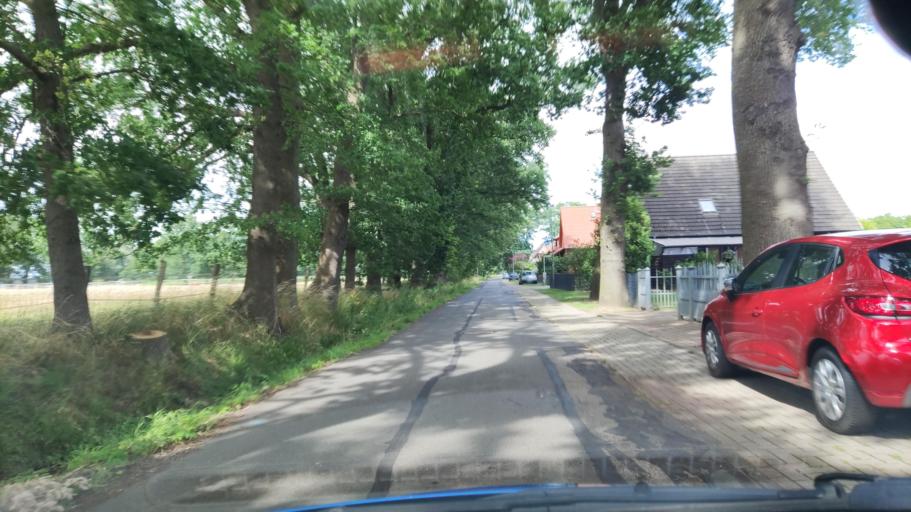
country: DE
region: Lower Saxony
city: Stelle
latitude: 53.4128
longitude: 10.0662
